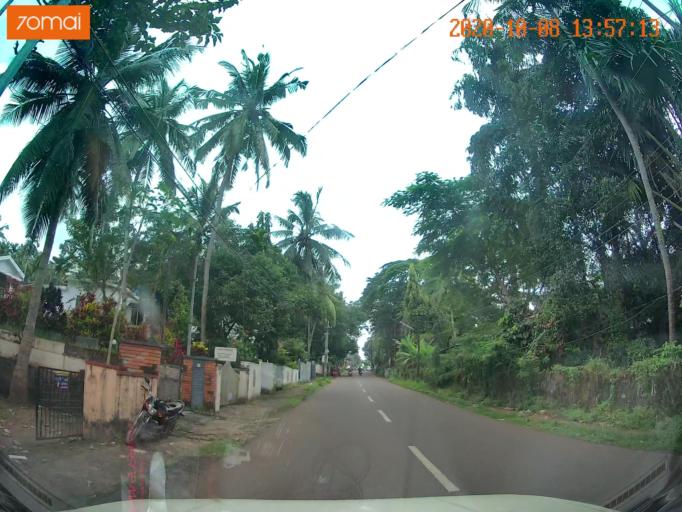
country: IN
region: Kerala
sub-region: Kozhikode
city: Kozhikode
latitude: 11.2892
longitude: 75.8015
